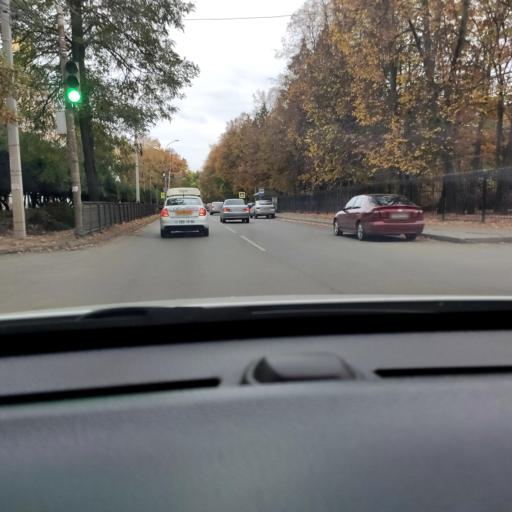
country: RU
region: Voronezj
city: Voronezh
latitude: 51.7194
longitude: 39.2199
